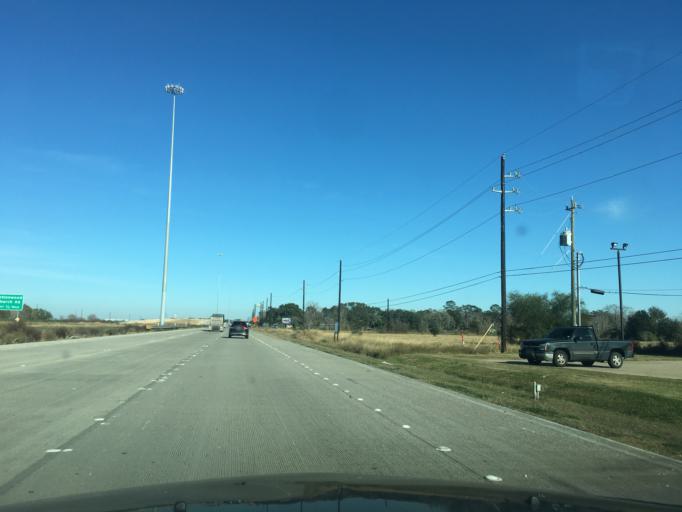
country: US
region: Texas
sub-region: Fort Bend County
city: Rosenberg
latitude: 29.5286
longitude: -95.8659
